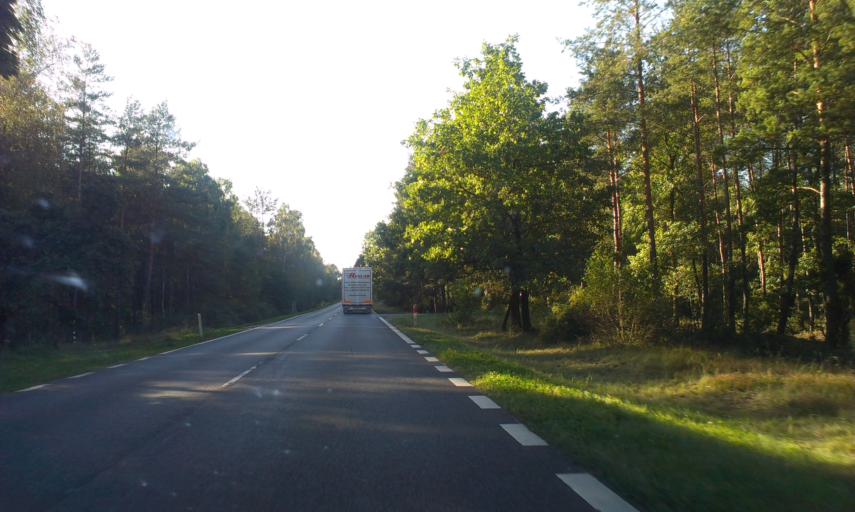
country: PL
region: Kujawsko-Pomorskie
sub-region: Powiat tucholski
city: Lubiewo
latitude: 53.4925
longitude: 18.0877
